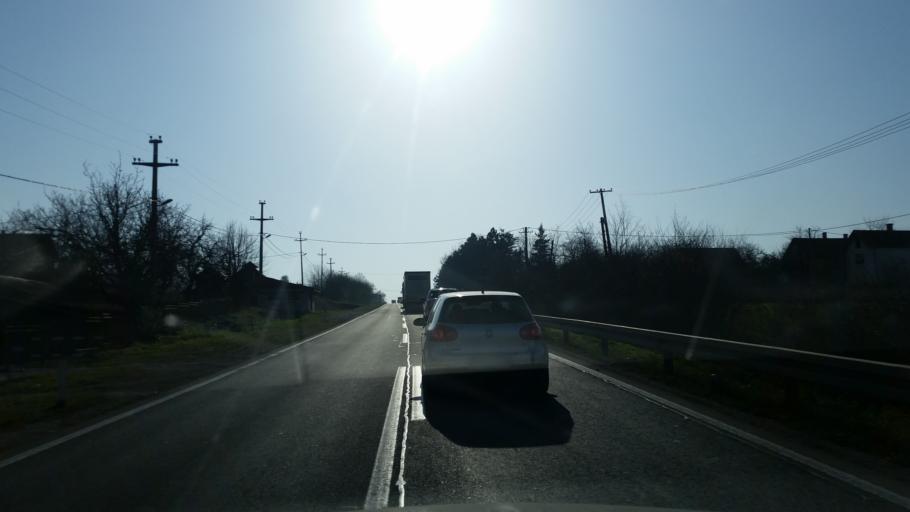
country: RS
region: Central Serbia
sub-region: Kolubarski Okrug
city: Lajkovac
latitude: 44.3564
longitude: 20.1899
